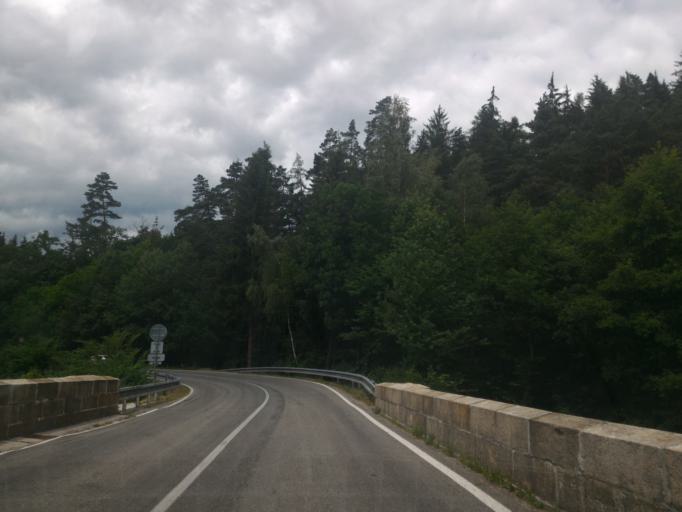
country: CZ
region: Vysocina
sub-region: Okres Pelhrimov
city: Zeliv
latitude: 49.5298
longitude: 15.1714
